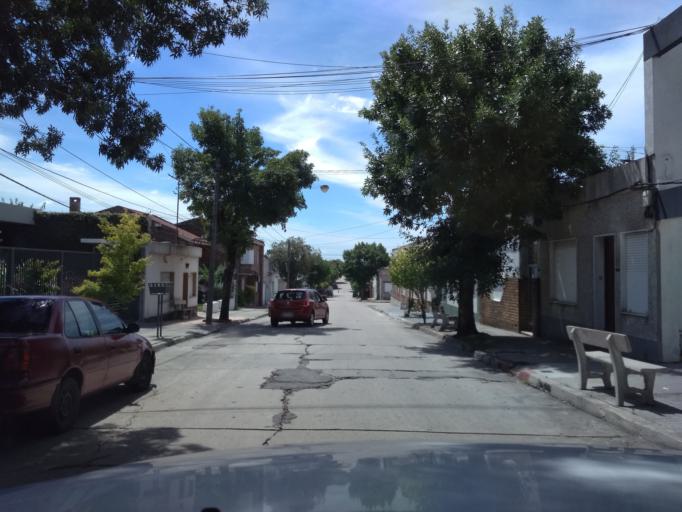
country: UY
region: Florida
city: Florida
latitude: -34.1008
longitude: -56.2173
